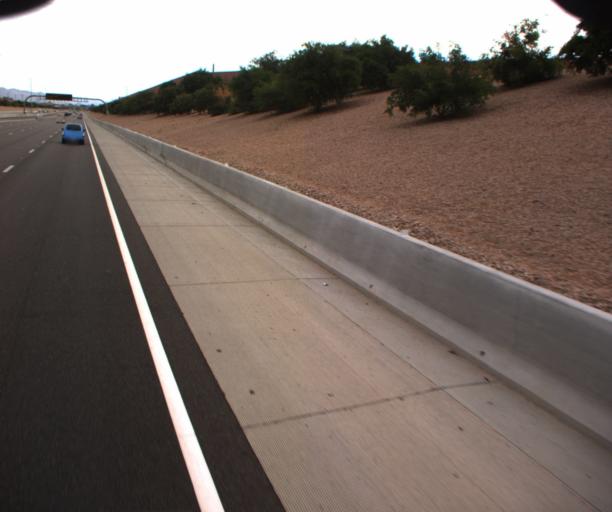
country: US
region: Arizona
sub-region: Maricopa County
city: Mesa
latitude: 33.4658
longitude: -111.8192
